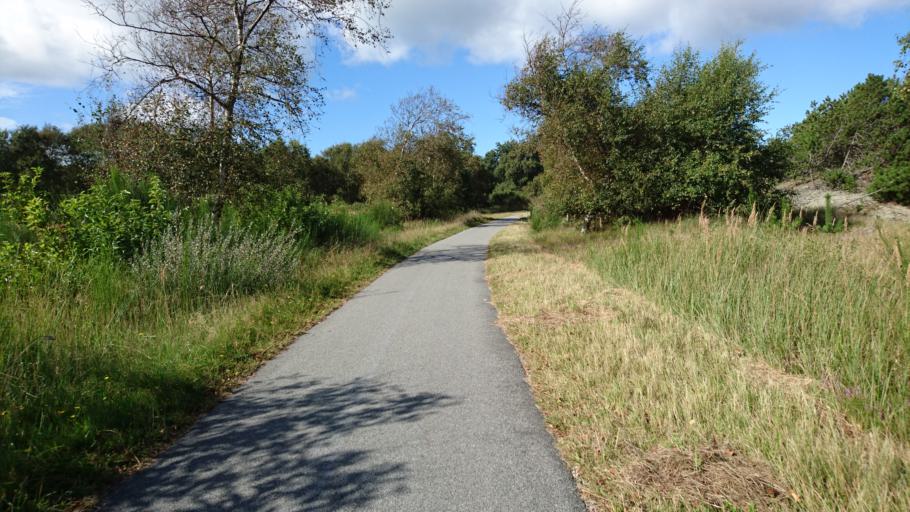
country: DK
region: North Denmark
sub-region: Frederikshavn Kommune
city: Skagen
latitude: 57.7085
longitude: 10.5231
